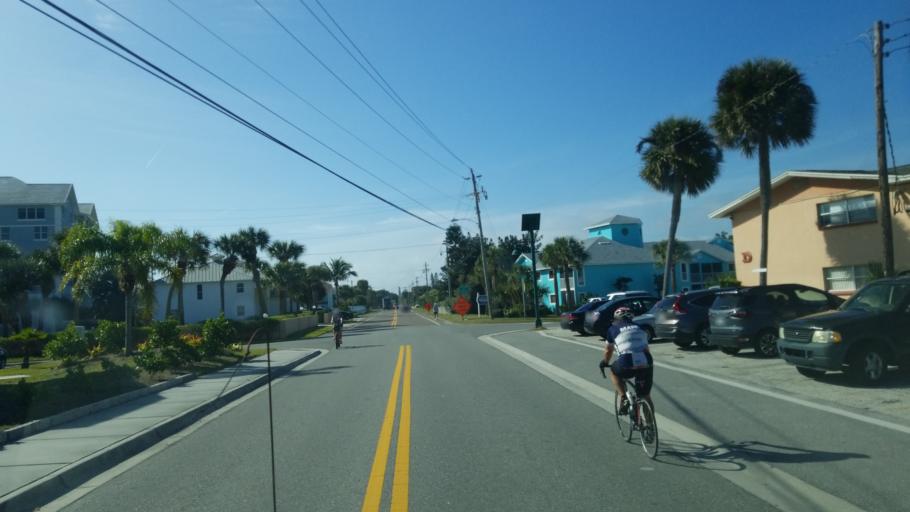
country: US
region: Florida
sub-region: Brevard County
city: Cape Canaveral
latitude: 28.3794
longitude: -80.6018
